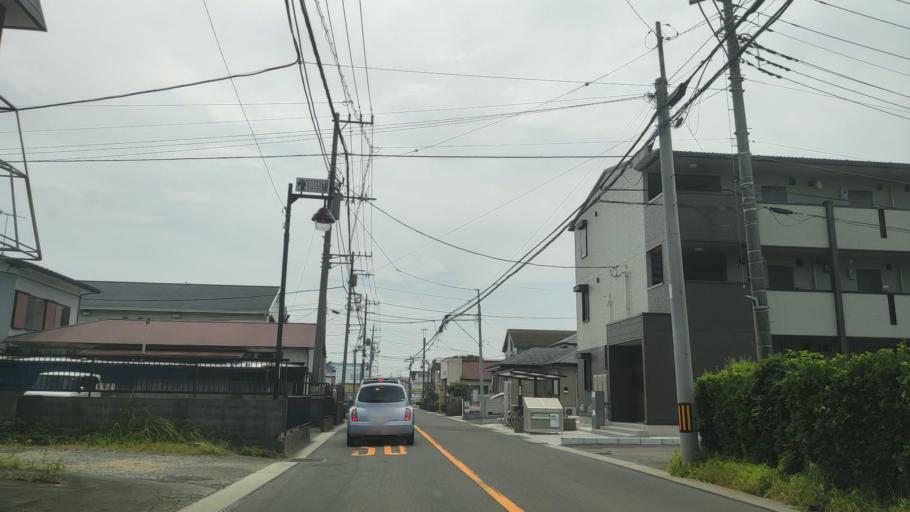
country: JP
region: Kanagawa
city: Zama
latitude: 35.4596
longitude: 139.3985
